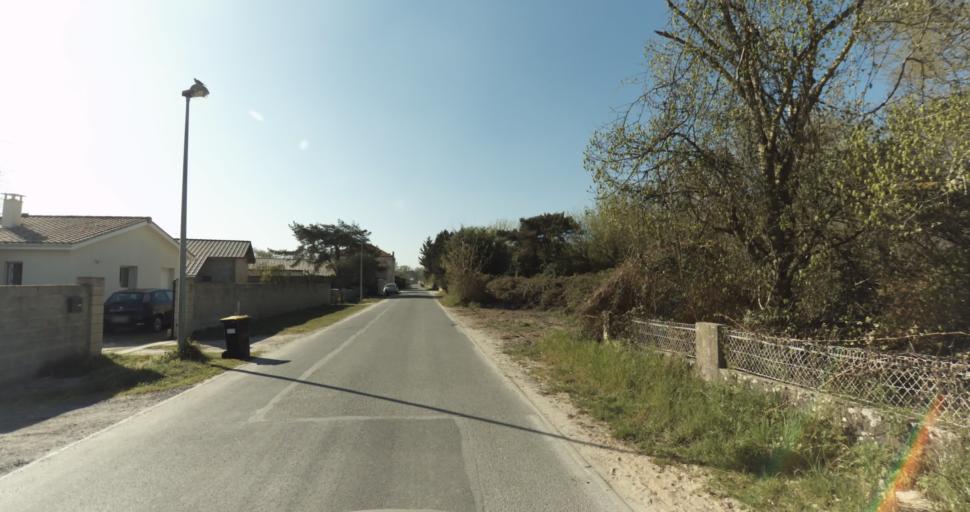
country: FR
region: Aquitaine
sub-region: Departement de la Gironde
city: Martignas-sur-Jalle
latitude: 44.8021
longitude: -0.8392
